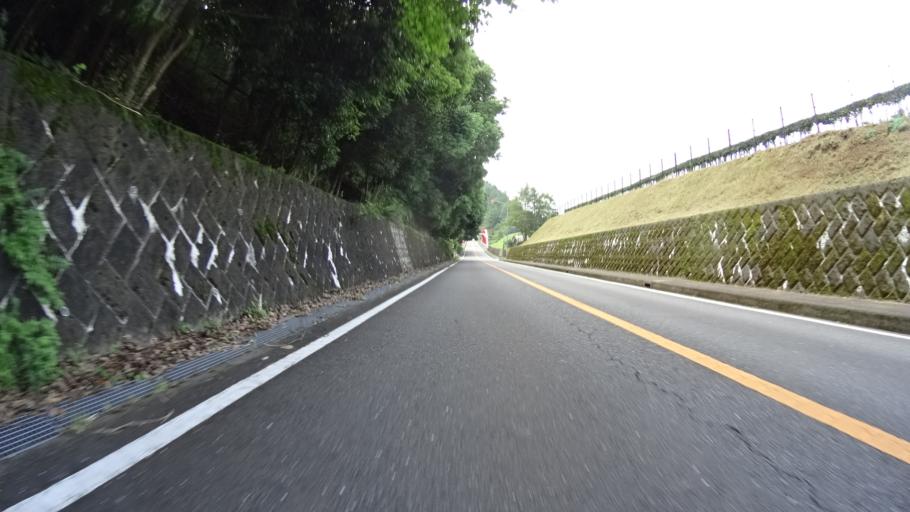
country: JP
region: Kanagawa
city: Hadano
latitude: 35.5075
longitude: 139.2308
